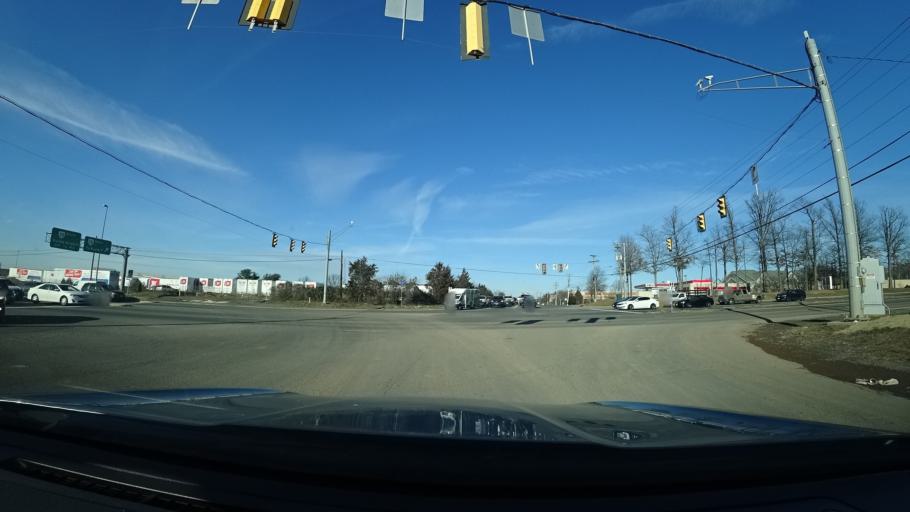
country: US
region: Virginia
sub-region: Loudoun County
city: Oak Grove
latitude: 38.9787
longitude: -77.4244
